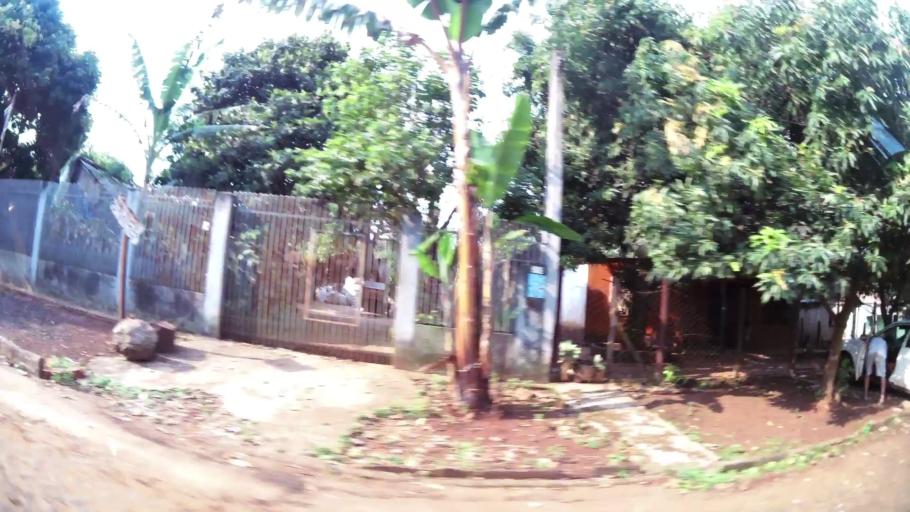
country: PY
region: Alto Parana
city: Ciudad del Este
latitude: -25.4862
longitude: -54.6511
